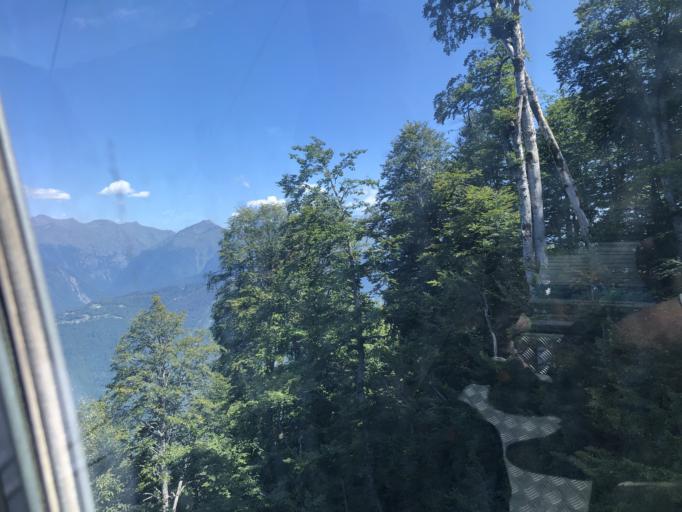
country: RU
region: Krasnodarskiy
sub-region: Sochi City
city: Krasnaya Polyana
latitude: 43.6568
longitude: 40.2516
